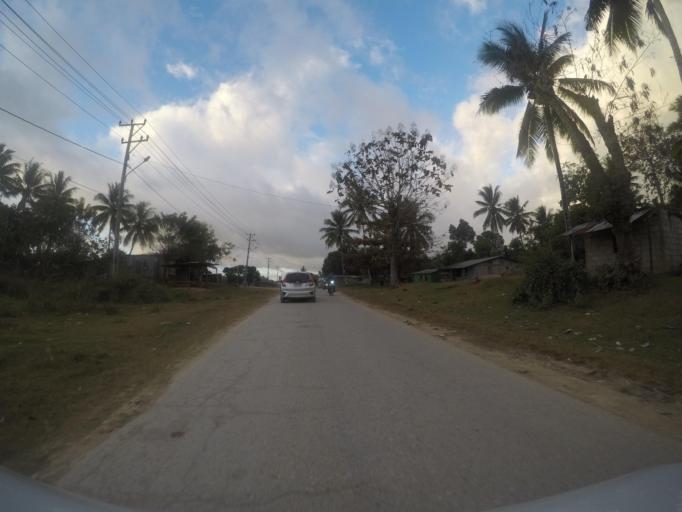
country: TL
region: Lautem
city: Lospalos
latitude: -8.5092
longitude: 126.9870
